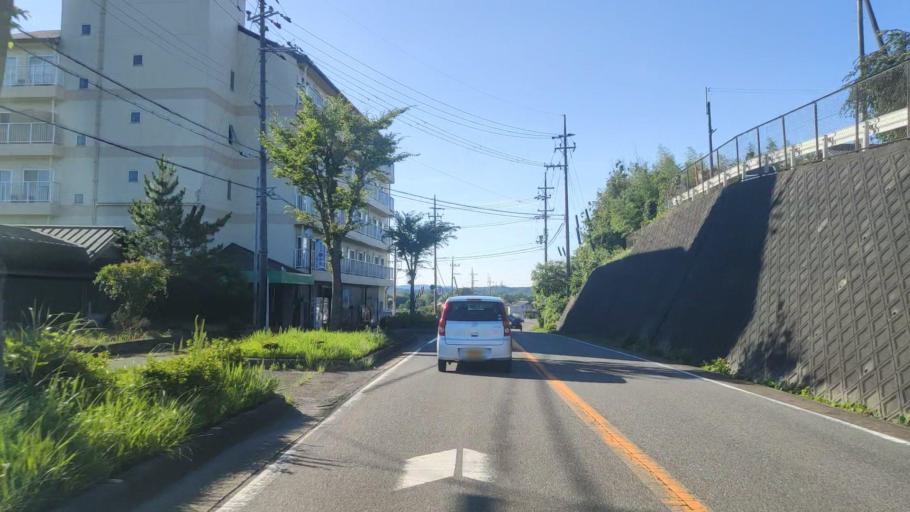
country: JP
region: Shiga Prefecture
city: Hino
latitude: 35.0430
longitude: 136.2412
